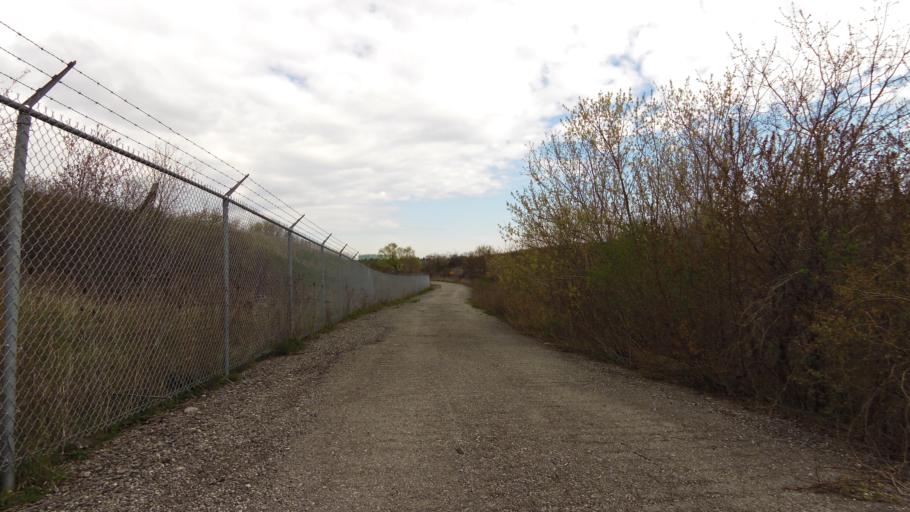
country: CA
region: Ontario
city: Etobicoke
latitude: 43.6614
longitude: -79.6291
